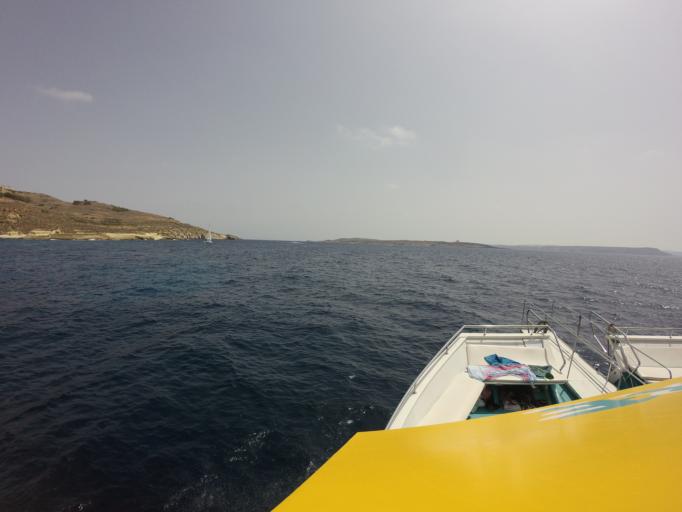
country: MT
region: Ghajnsielem
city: Mgarr
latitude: 36.0248
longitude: 14.3023
